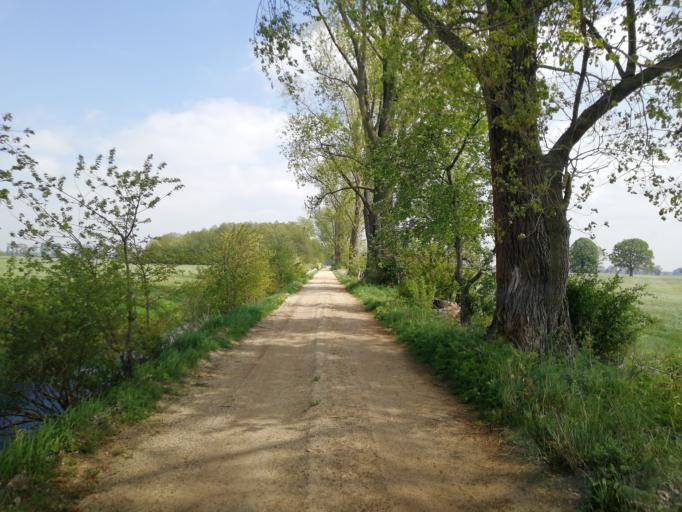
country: DE
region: Brandenburg
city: Doberlug-Kirchhain
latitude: 51.6752
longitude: 13.5403
